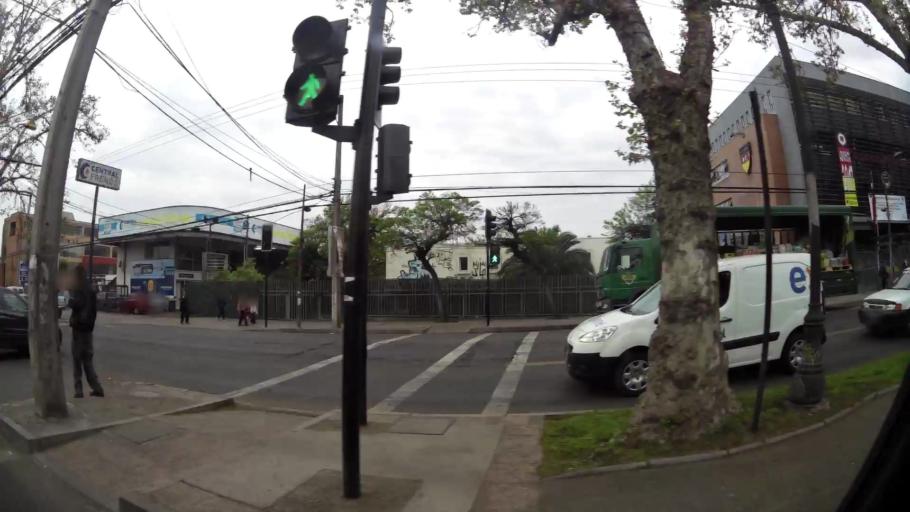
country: CL
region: Santiago Metropolitan
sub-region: Provincia de Santiago
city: Lo Prado
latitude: -33.5013
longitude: -70.7574
